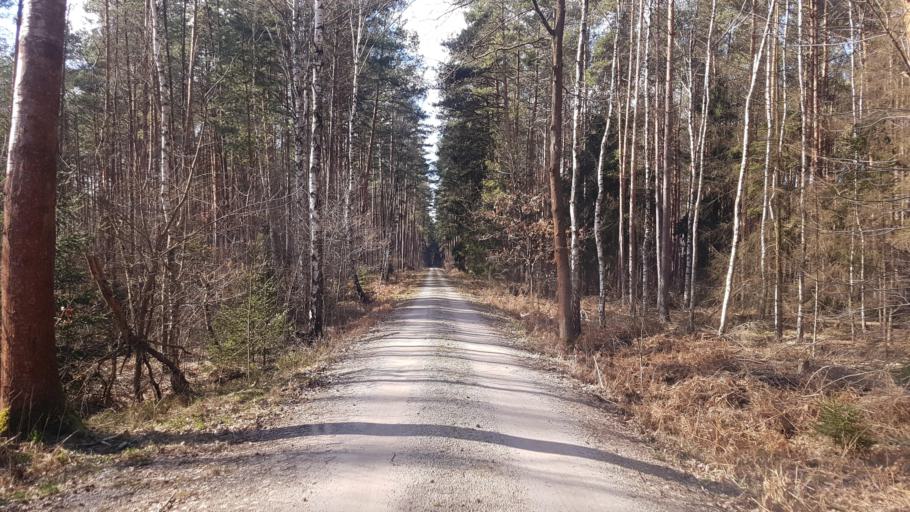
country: DE
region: Brandenburg
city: Plessa
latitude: 51.5160
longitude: 13.6020
